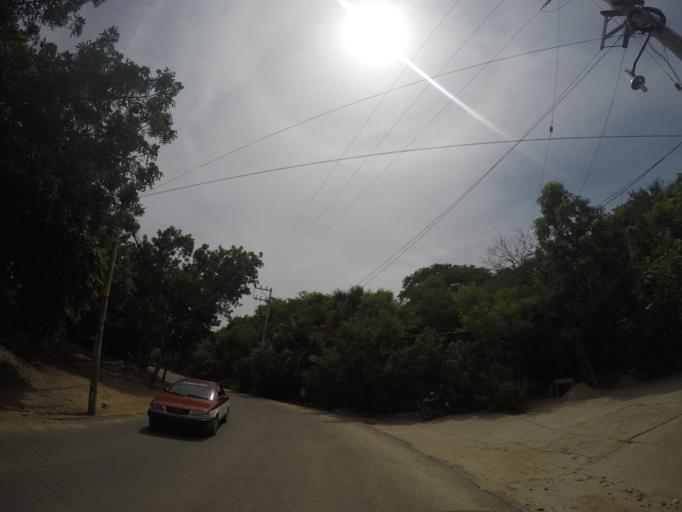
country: MX
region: Oaxaca
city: San Pedro Pochutla
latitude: 15.6649
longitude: -96.5015
